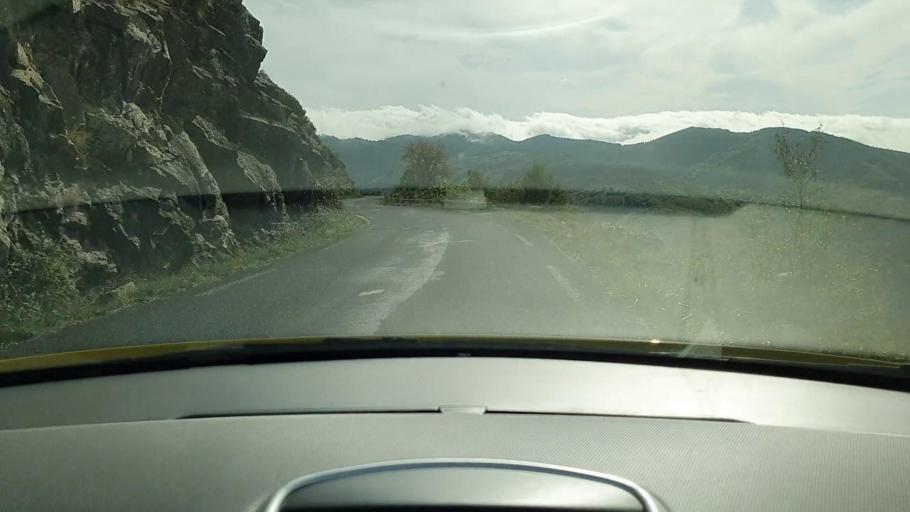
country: FR
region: Languedoc-Roussillon
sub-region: Departement de la Lozere
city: Meyrueis
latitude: 44.0676
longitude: 3.4185
